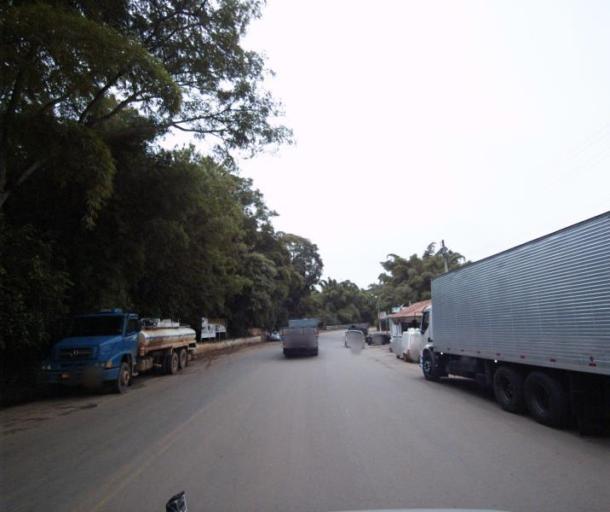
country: BR
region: Goias
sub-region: Pirenopolis
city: Pirenopolis
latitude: -15.9177
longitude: -48.8089
